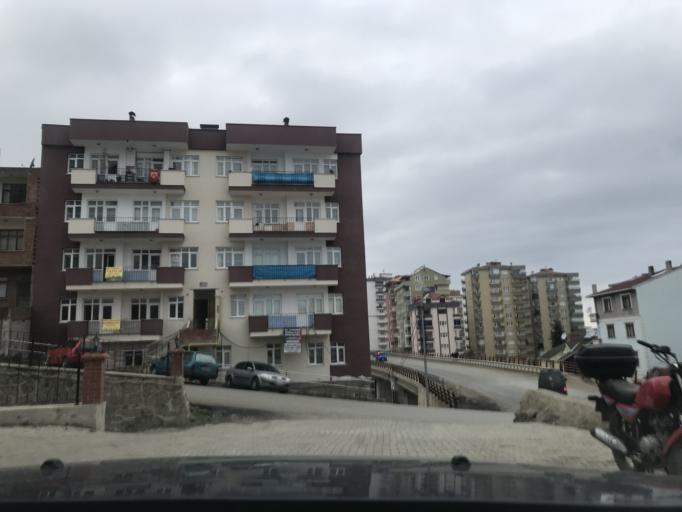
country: TR
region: Trabzon
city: Akcaabat
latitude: 41.0088
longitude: 39.6042
